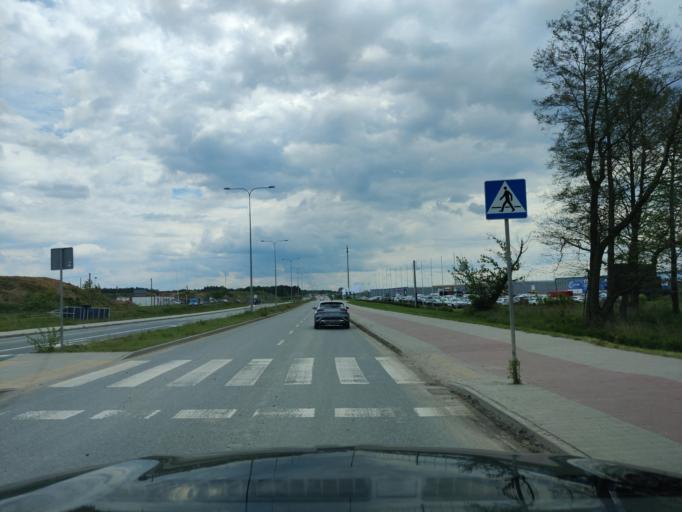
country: PL
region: Masovian Voivodeship
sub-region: Powiat pruszkowski
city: Nadarzyn
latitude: 52.1123
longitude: 20.8317
